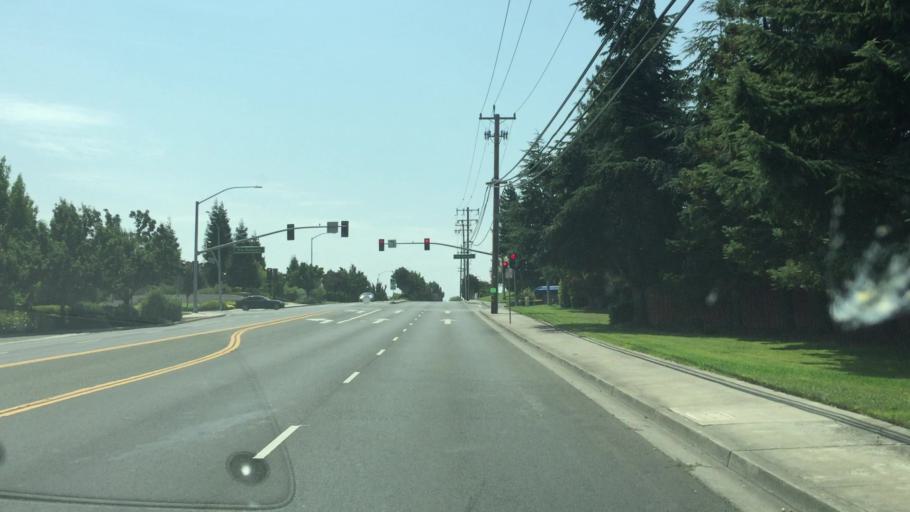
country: US
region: California
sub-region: Napa County
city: American Canyon
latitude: 38.1585
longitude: -122.2391
